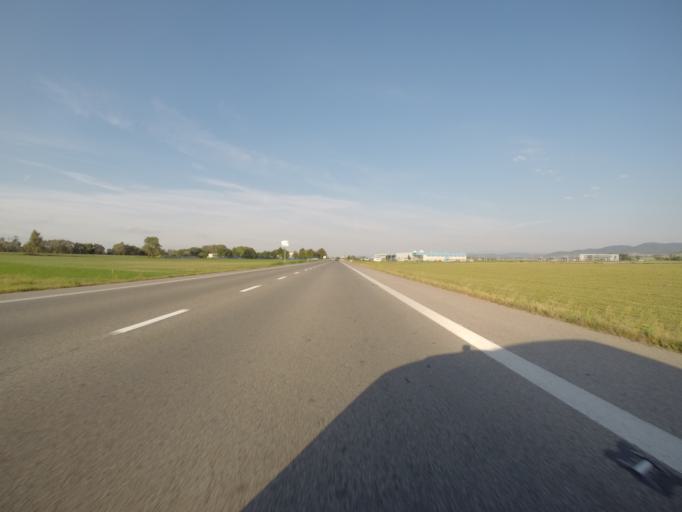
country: SK
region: Nitriansky
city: Banovce nad Bebravou
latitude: 48.5573
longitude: 18.1927
